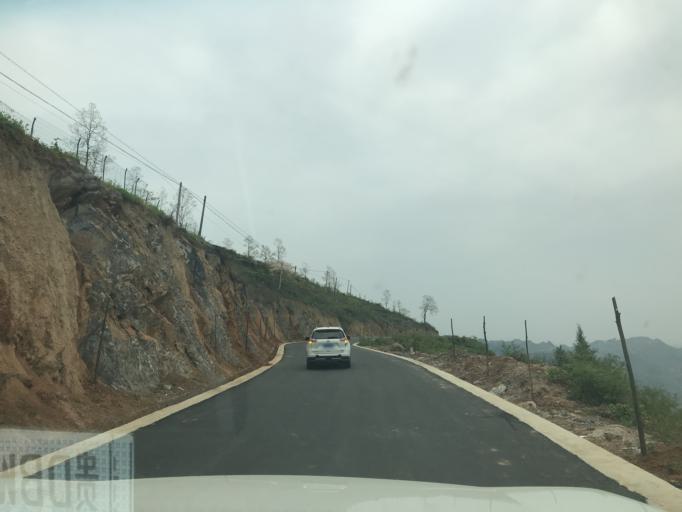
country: CN
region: Guizhou Sheng
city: Tongjing
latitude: 28.3081
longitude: 108.2764
